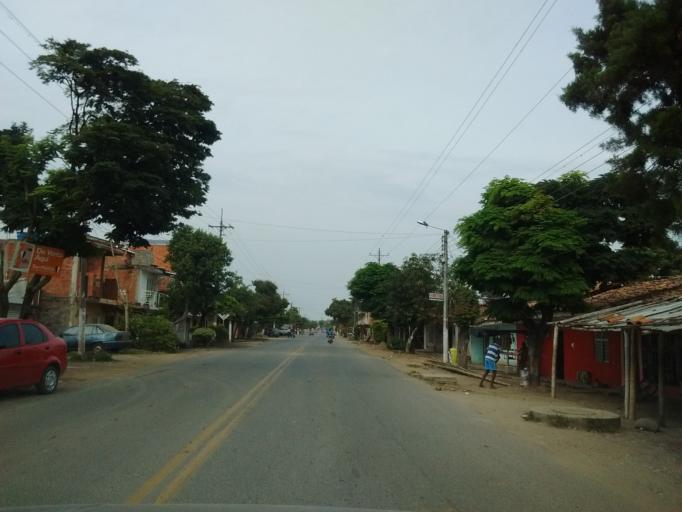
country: CO
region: Cauca
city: Puerto Tejada
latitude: 3.1783
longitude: -76.4550
